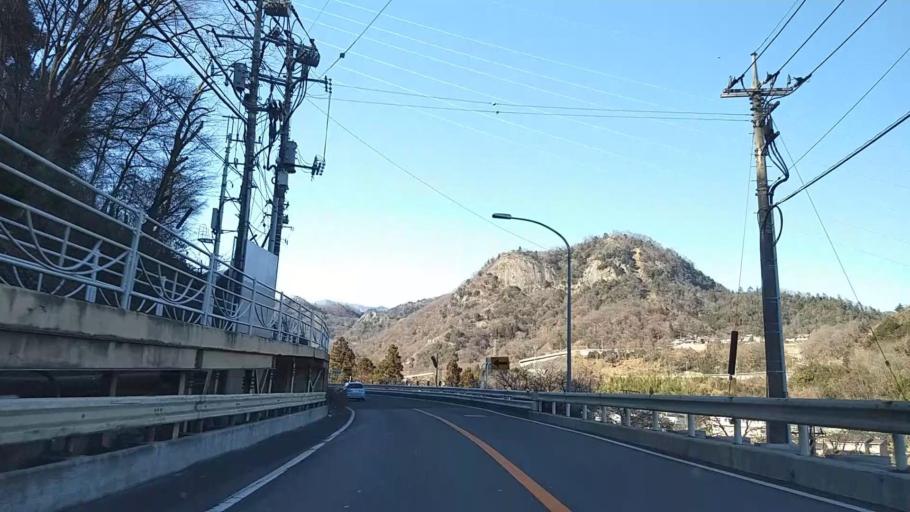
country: JP
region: Yamanashi
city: Otsuki
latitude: 35.6126
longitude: 138.9589
